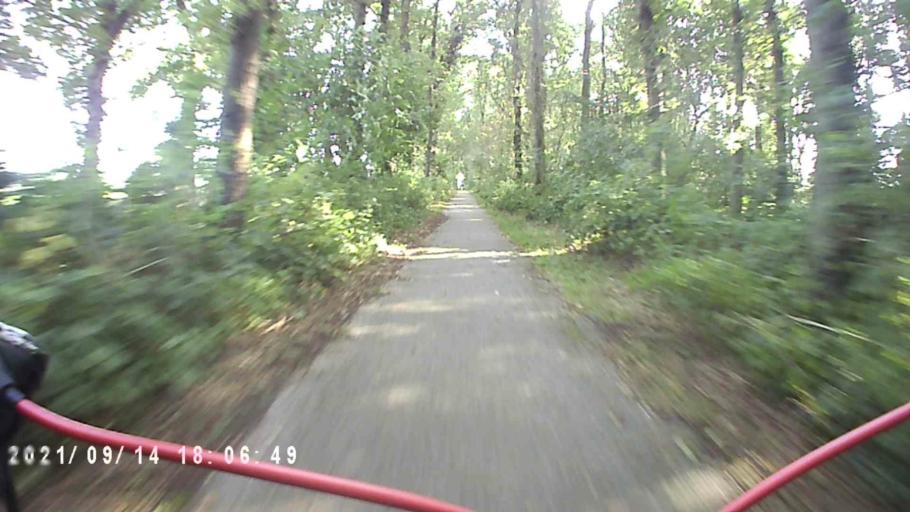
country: NL
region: Drenthe
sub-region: Gemeente Tynaarlo
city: Zuidlaren
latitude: 53.1062
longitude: 6.6559
